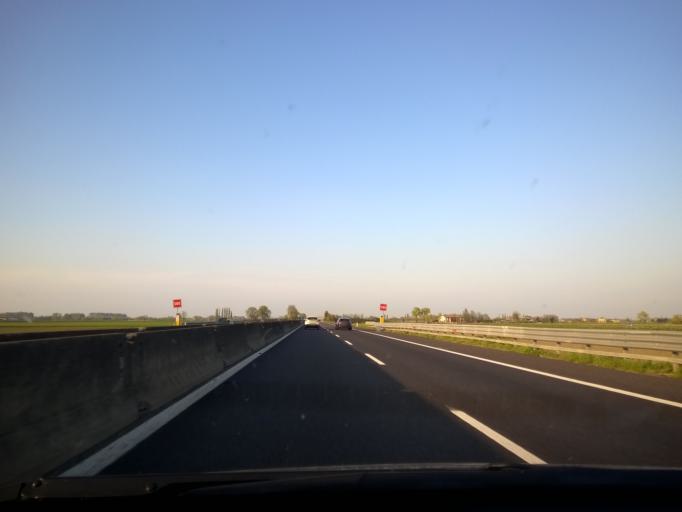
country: IT
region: Emilia-Romagna
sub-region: Provincia di Bologna
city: Bentivoglio
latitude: 44.6389
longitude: 11.4347
